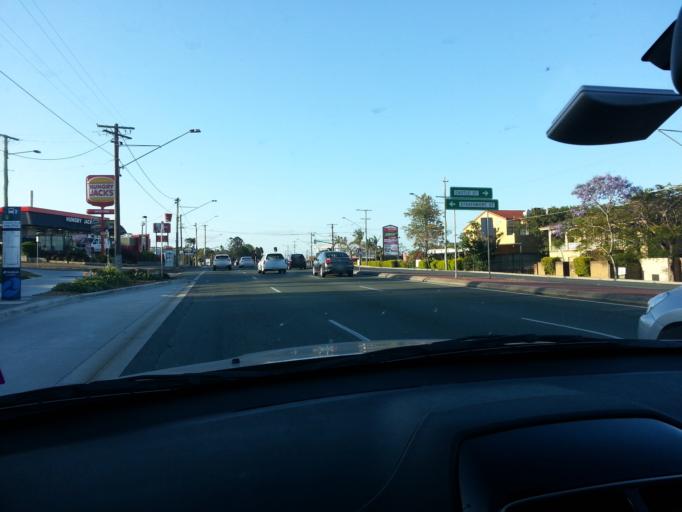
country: AU
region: Queensland
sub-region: Brisbane
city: Gordon Park
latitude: -27.4052
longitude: 153.0320
